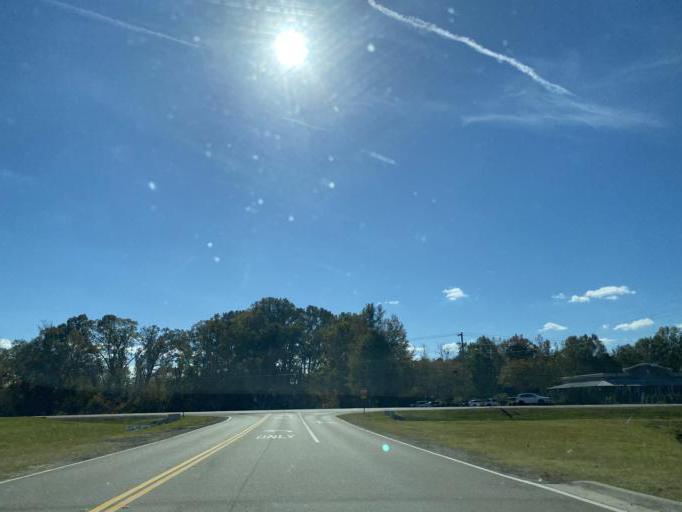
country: US
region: Mississippi
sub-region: Madison County
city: Madison
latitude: 32.4585
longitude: -90.1276
